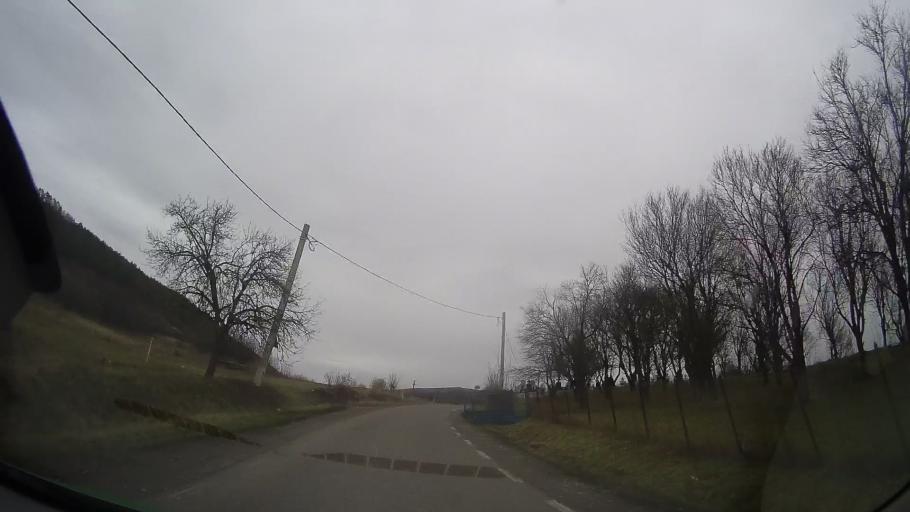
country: RO
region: Mures
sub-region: Comuna Bala
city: Bala
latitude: 46.7150
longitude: 24.5047
